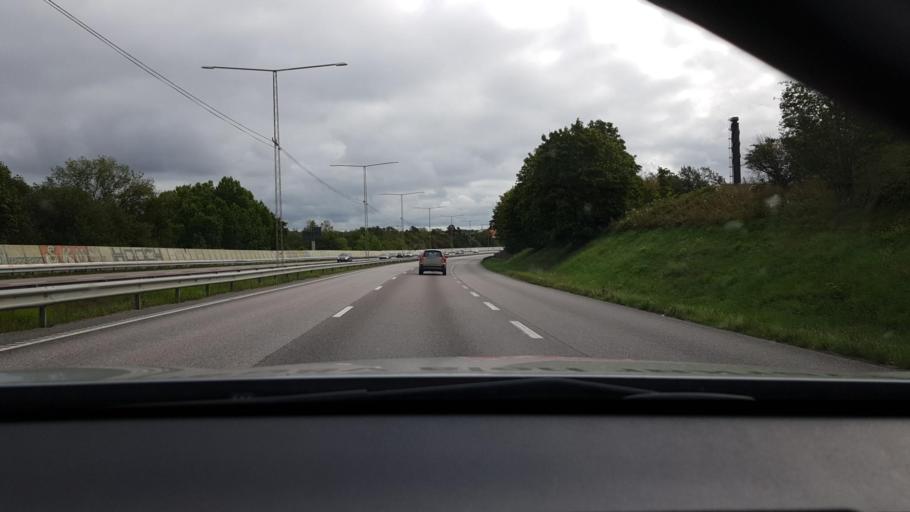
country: SE
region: Stockholm
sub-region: Lidingo
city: Brevik
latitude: 59.3166
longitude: 18.2013
